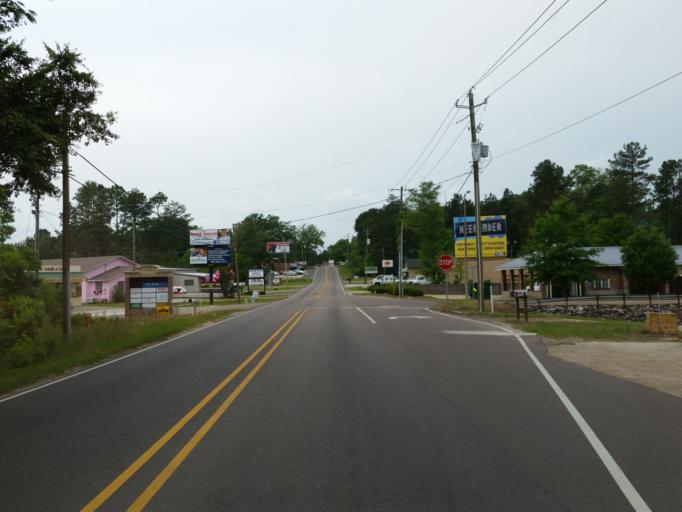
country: US
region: Mississippi
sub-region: Lamar County
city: West Hattiesburg
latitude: 31.3189
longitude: -89.3612
